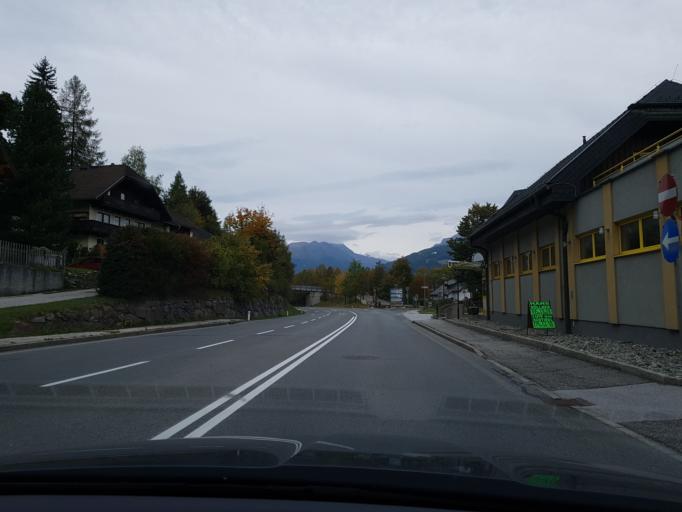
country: AT
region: Salzburg
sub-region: Politischer Bezirk Tamsweg
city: Tamsweg
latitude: 47.1231
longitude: 13.8069
